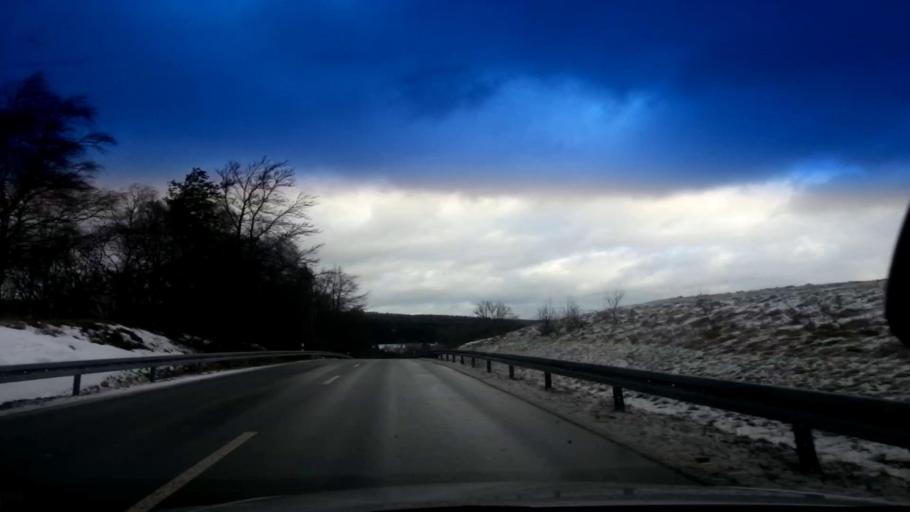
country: DE
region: Bavaria
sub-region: Upper Franconia
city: Weissenstadt
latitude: 50.1145
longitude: 11.8990
